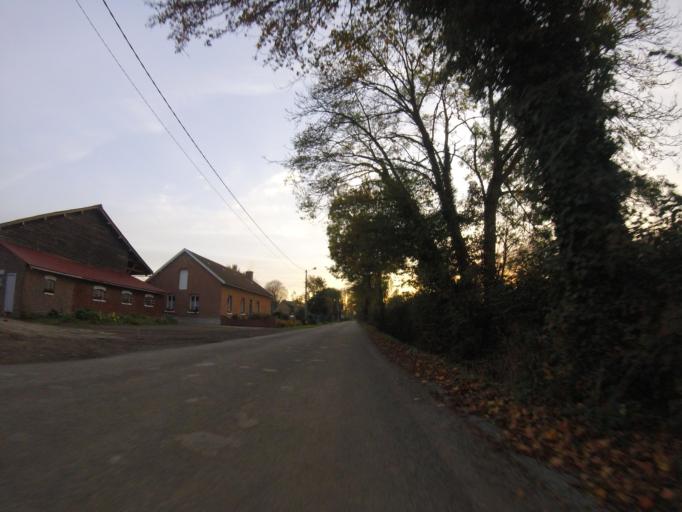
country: FR
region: Nord-Pas-de-Calais
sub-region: Departement du Pas-de-Calais
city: Sailly-sur-la-Lys
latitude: 50.6480
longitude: 2.7923
